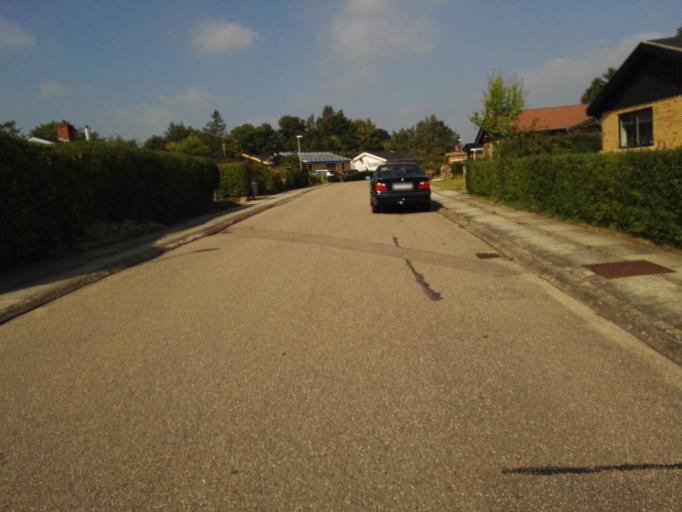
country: DK
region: Capital Region
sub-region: Egedal Kommune
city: Stenlose
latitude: 55.7624
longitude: 12.1927
